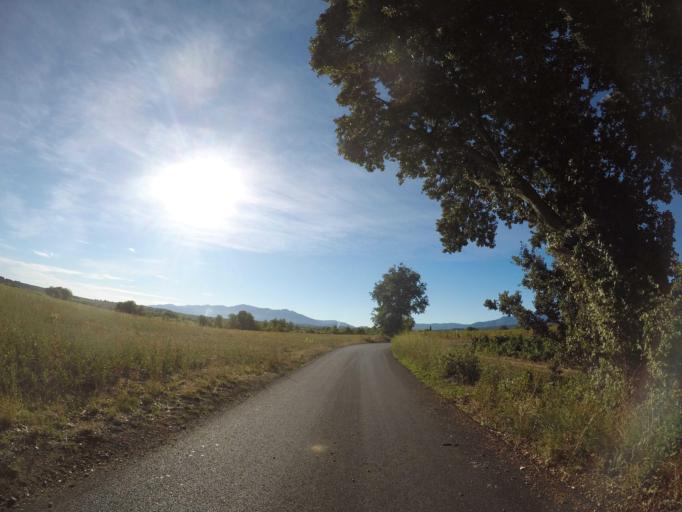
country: FR
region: Languedoc-Roussillon
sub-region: Departement des Pyrenees-Orientales
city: Llupia
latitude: 42.5976
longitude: 2.7628
